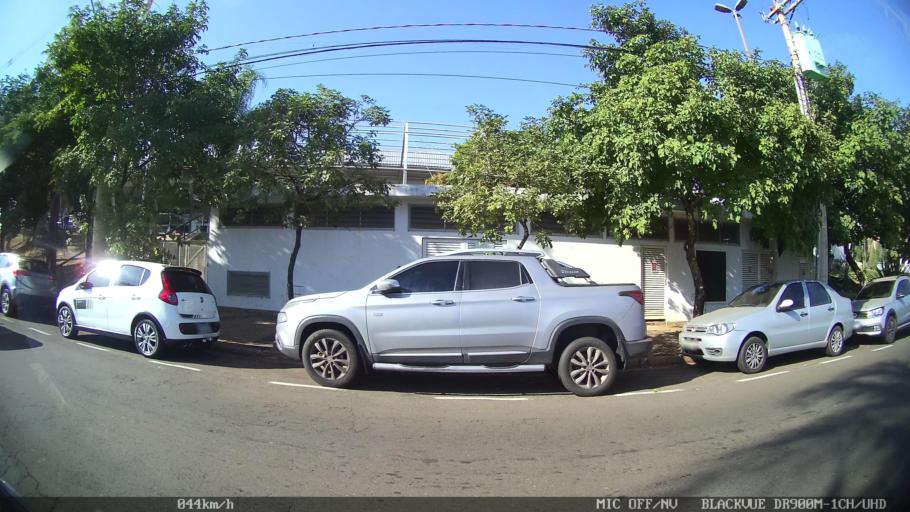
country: BR
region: Sao Paulo
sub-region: Sao Jose Do Rio Preto
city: Sao Jose do Rio Preto
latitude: -20.8119
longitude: -49.4050
